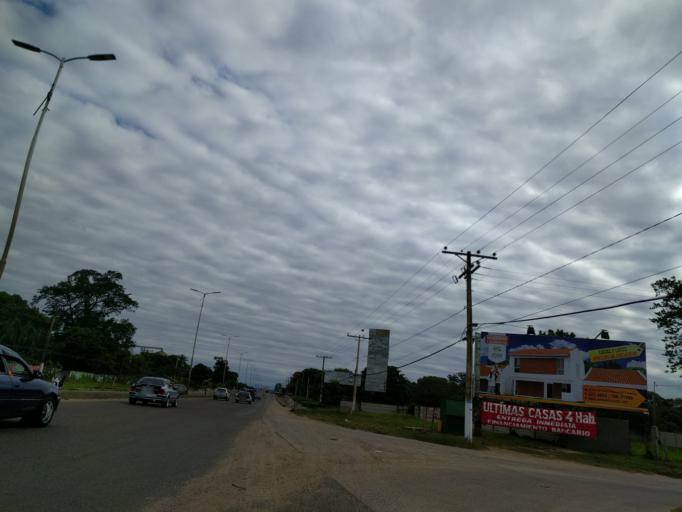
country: BO
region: Santa Cruz
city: Santa Cruz de la Sierra
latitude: -17.8549
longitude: -63.2571
